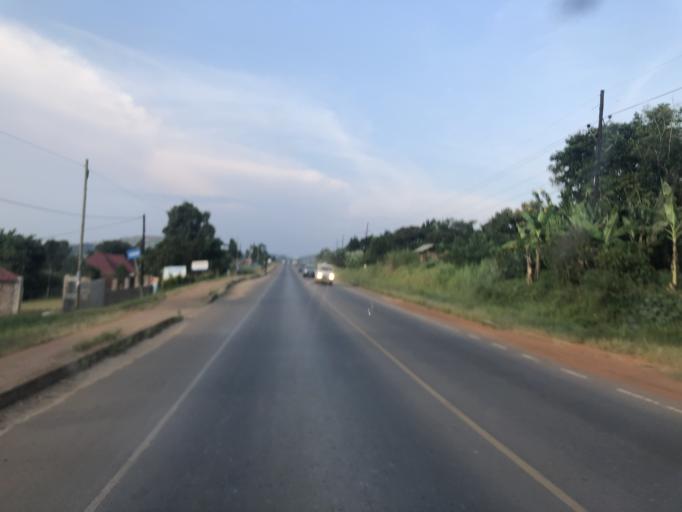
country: UG
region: Central Region
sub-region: Mpigi District
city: Mpigi
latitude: 0.1771
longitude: 32.2772
